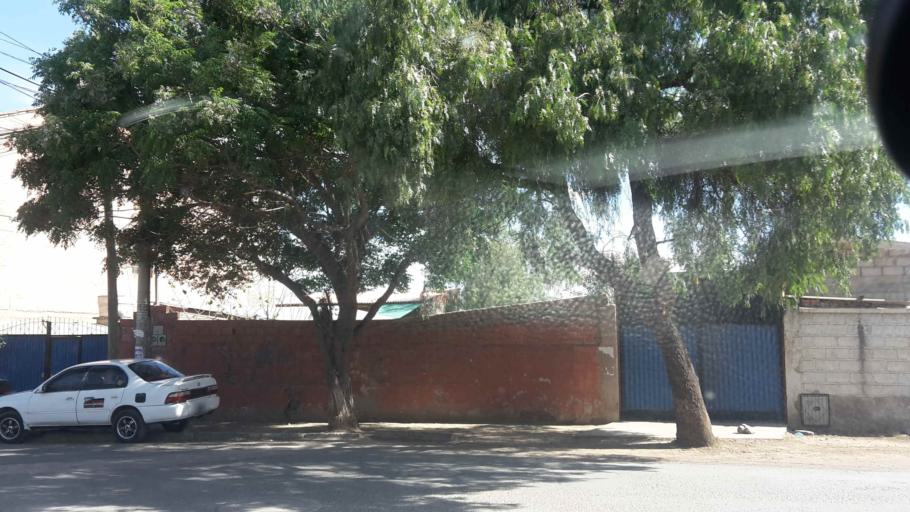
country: BO
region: Cochabamba
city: Cochabamba
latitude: -17.3371
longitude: -66.2263
